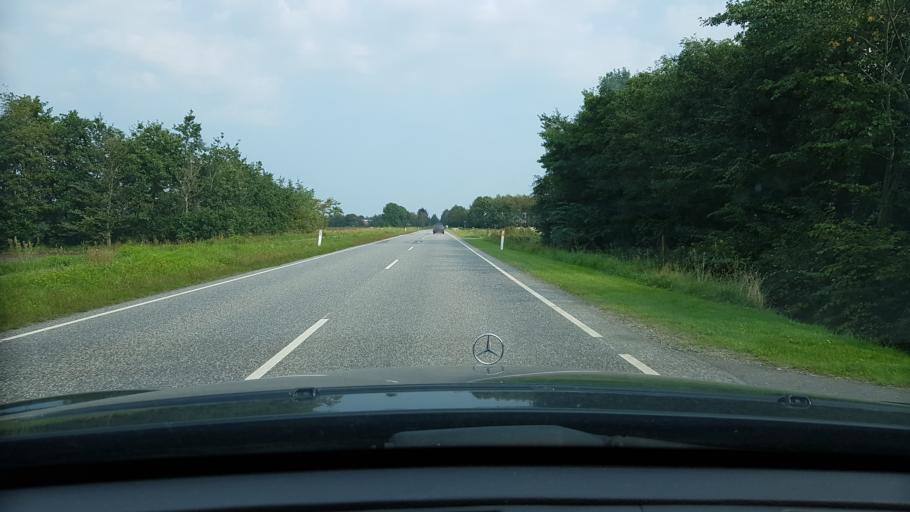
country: DK
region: North Denmark
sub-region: Alborg Kommune
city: Storvorde
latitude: 56.9924
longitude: 10.1498
